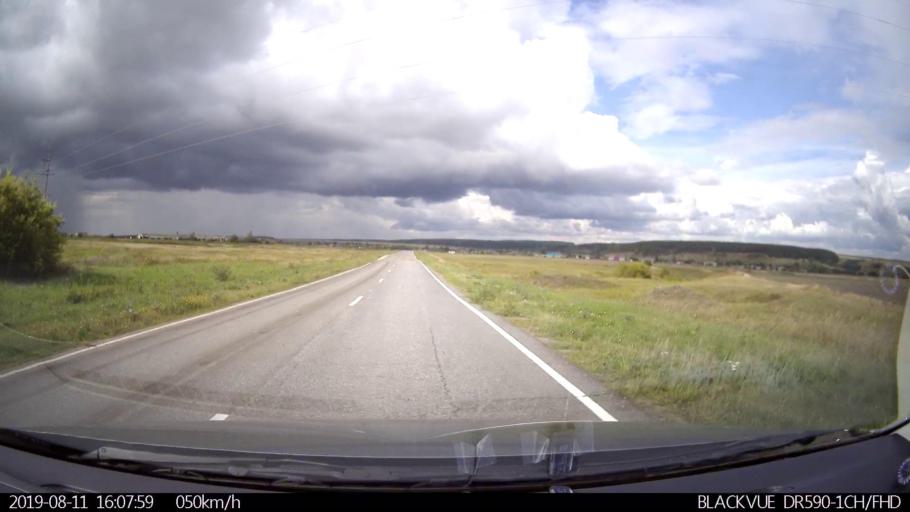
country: RU
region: Ulyanovsk
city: Ignatovka
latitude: 53.9812
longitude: 47.6472
